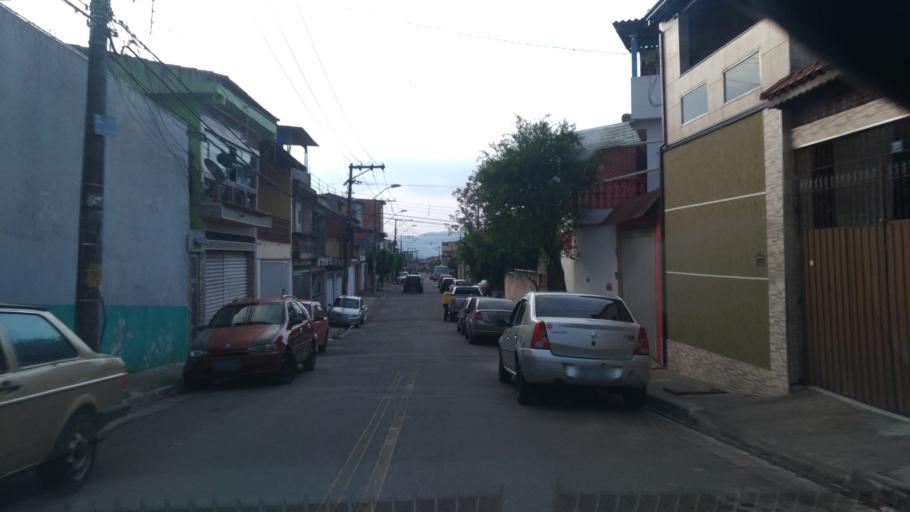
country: BR
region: Sao Paulo
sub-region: Itaquaquecetuba
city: Itaquaquecetuba
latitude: -23.4328
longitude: -46.4300
